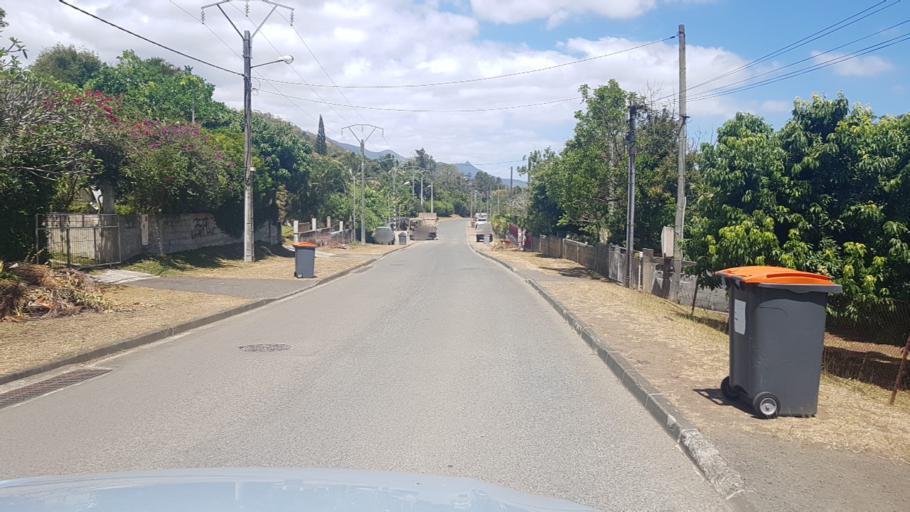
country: NC
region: South Province
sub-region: Dumbea
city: Dumbea
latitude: -22.1324
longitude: 166.4300
